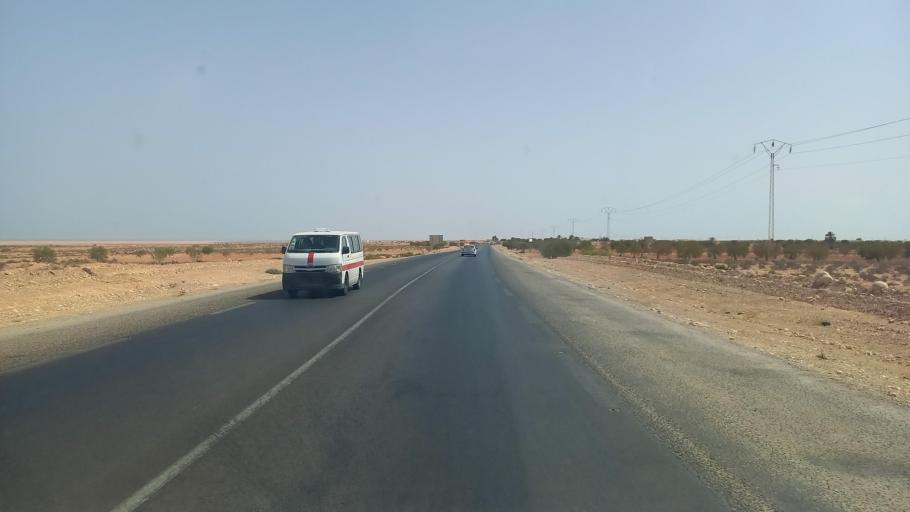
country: TN
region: Madanin
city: Medenine
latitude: 33.3865
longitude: 10.7036
